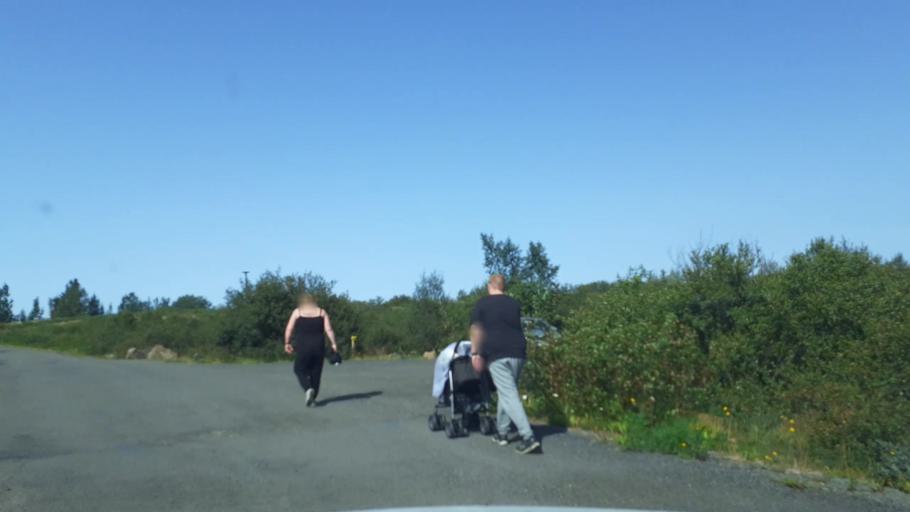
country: IS
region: West
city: Borgarnes
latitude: 64.7023
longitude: -21.6187
